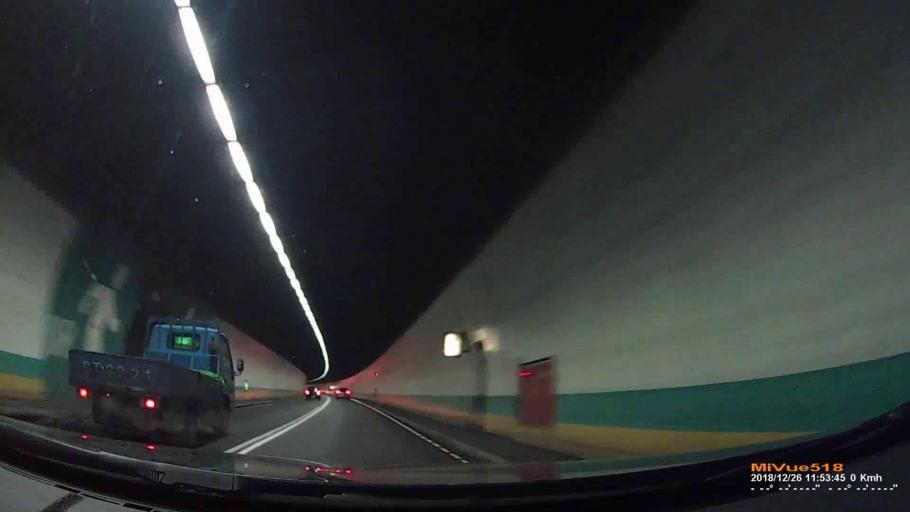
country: TW
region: Taiwan
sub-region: Keelung
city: Keelung
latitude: 24.9559
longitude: 121.6949
